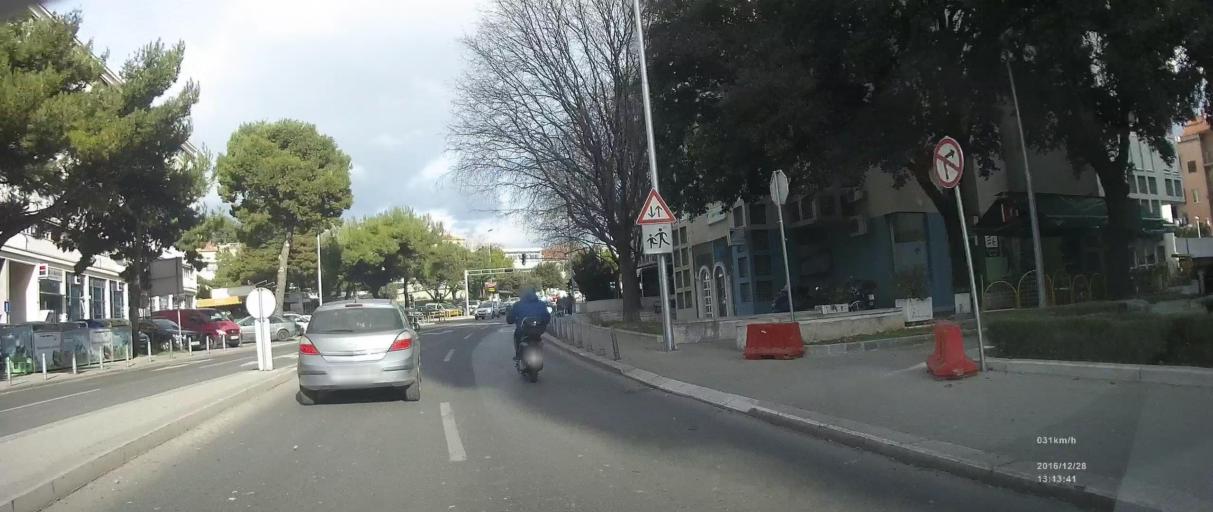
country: HR
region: Splitsko-Dalmatinska
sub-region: Grad Split
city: Split
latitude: 43.5060
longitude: 16.4481
